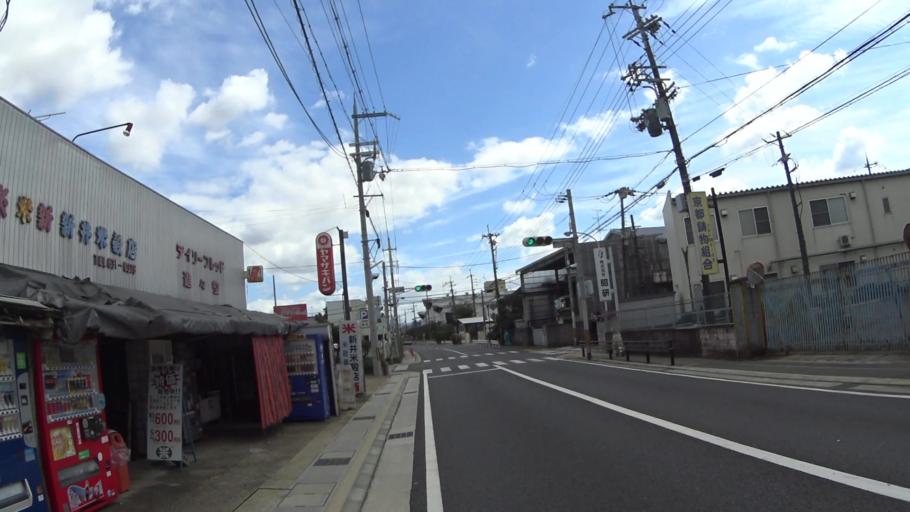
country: JP
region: Kyoto
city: Yawata
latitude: 34.8875
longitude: 135.7230
